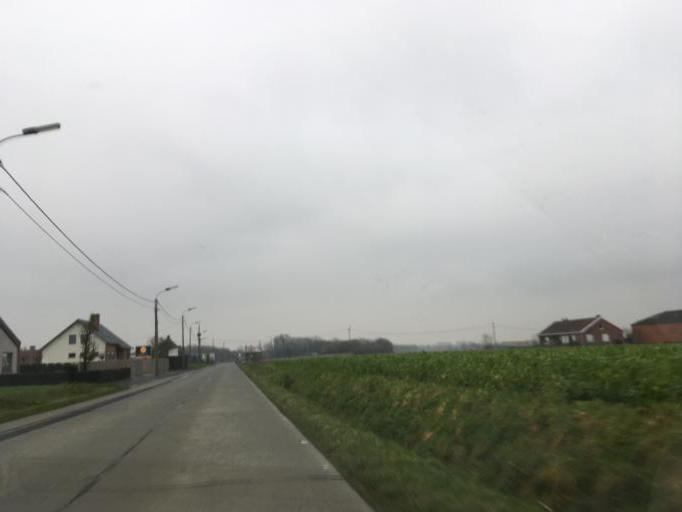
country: BE
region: Flanders
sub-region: Provincie West-Vlaanderen
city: Izegem
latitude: 50.8882
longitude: 3.1698
